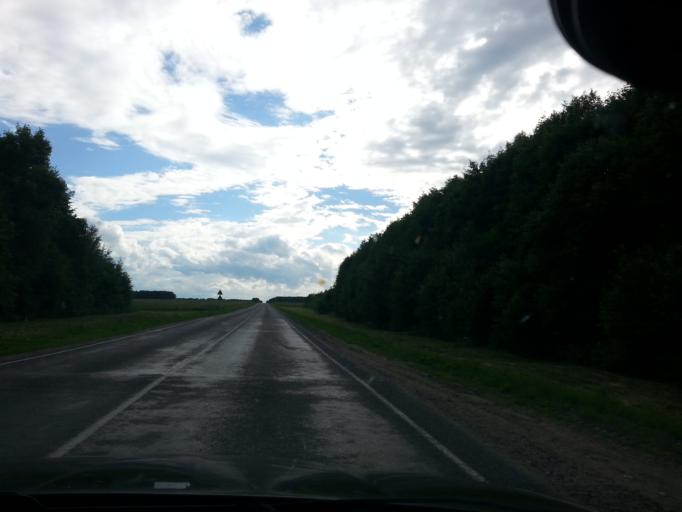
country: BY
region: Grodnenskaya
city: Astravyets
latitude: 54.8011
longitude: 26.1251
